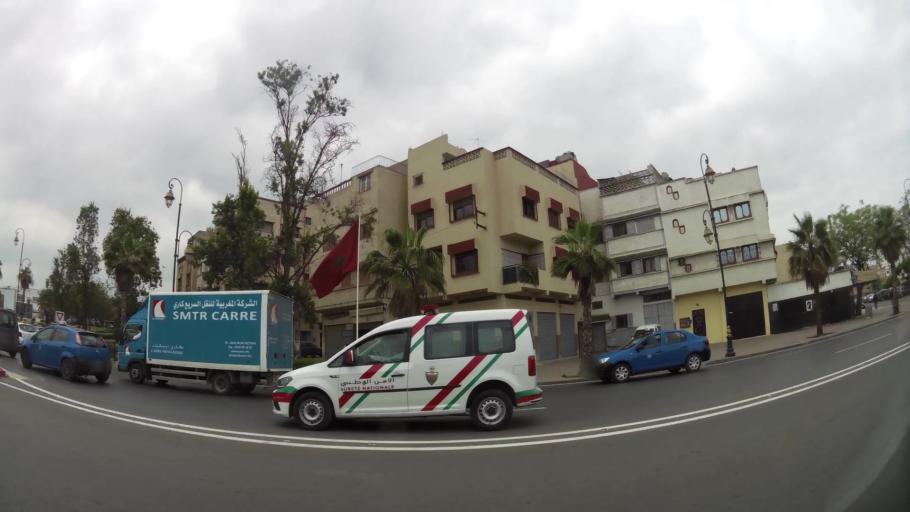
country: MA
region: Rabat-Sale-Zemmour-Zaer
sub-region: Rabat
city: Rabat
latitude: 33.9912
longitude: -6.8714
